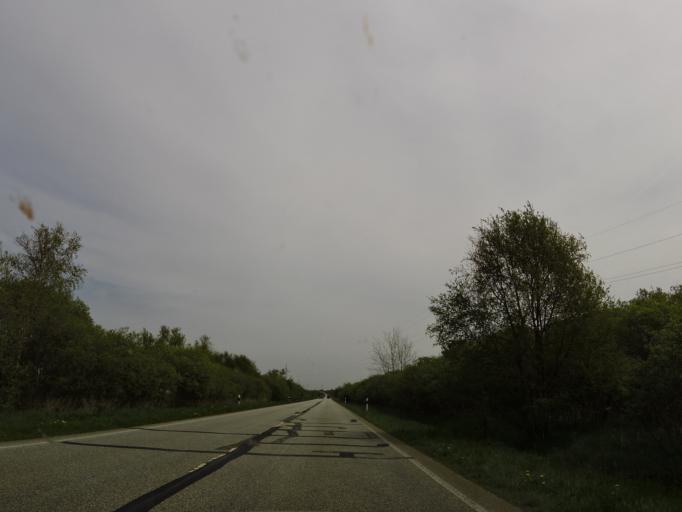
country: DE
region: Schleswig-Holstein
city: Husum
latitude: 54.4571
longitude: 9.0531
